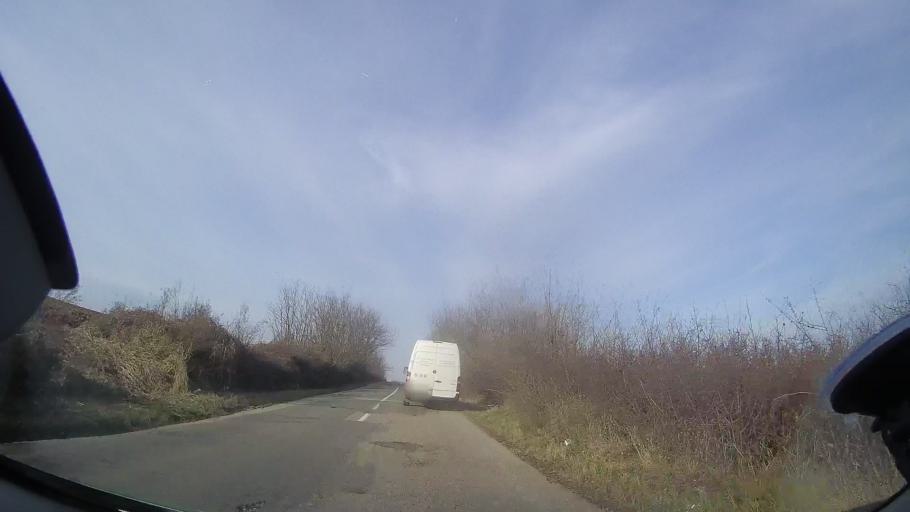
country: RO
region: Bihor
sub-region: Comuna Spinus
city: Spinus
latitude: 47.2080
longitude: 22.1807
